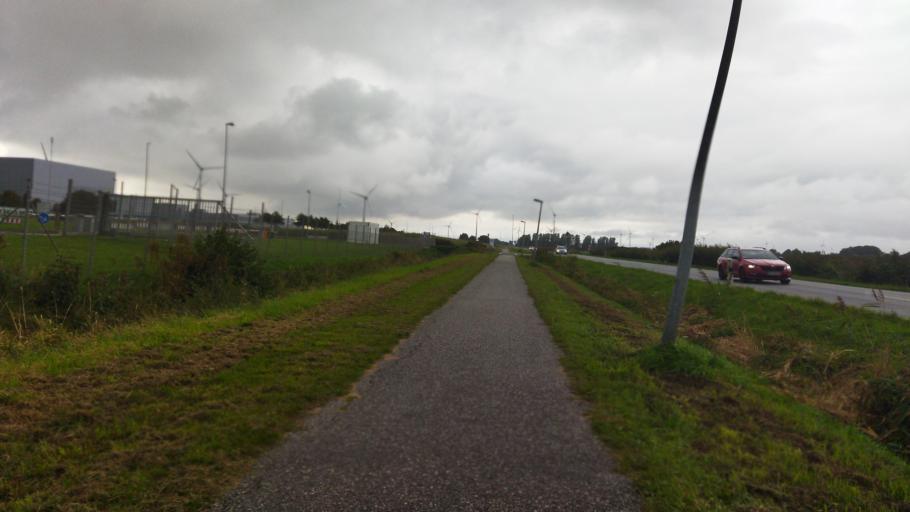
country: DE
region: Lower Saxony
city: Emden
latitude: 53.3580
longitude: 7.1488
